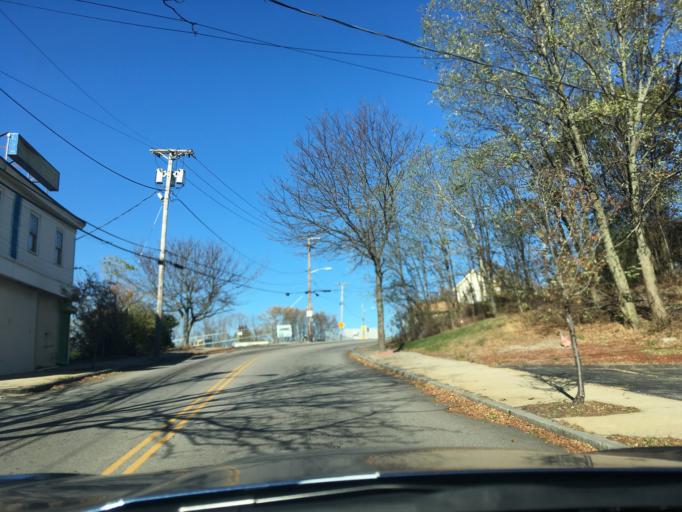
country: US
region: Rhode Island
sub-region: Providence County
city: Central Falls
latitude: 41.8895
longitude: -71.3816
